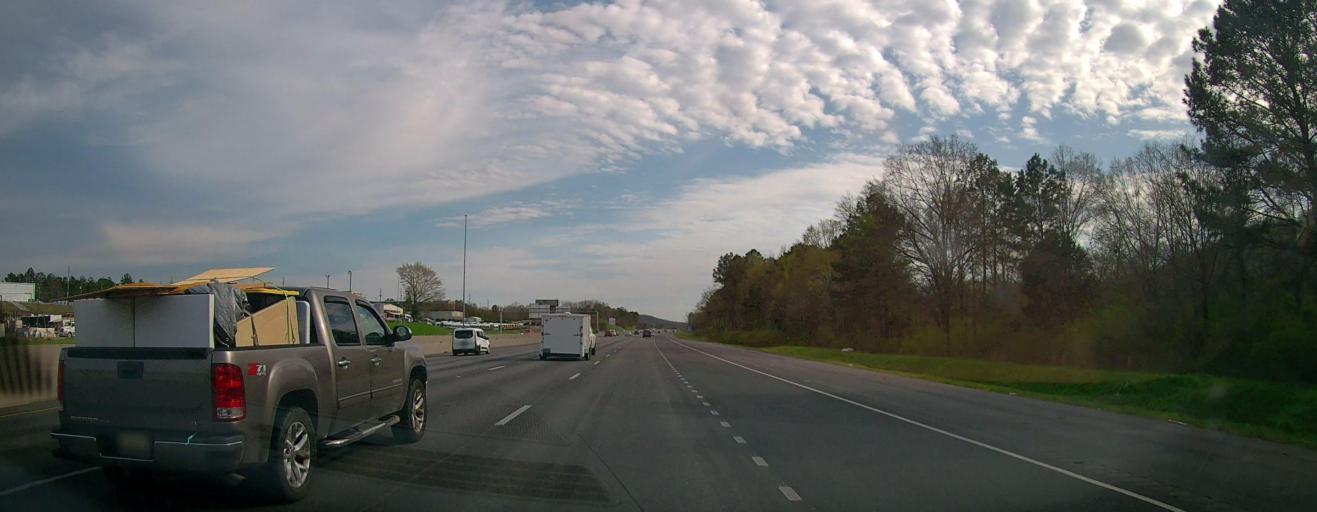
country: US
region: Alabama
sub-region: Shelby County
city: Pelham
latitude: 33.2764
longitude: -86.7999
